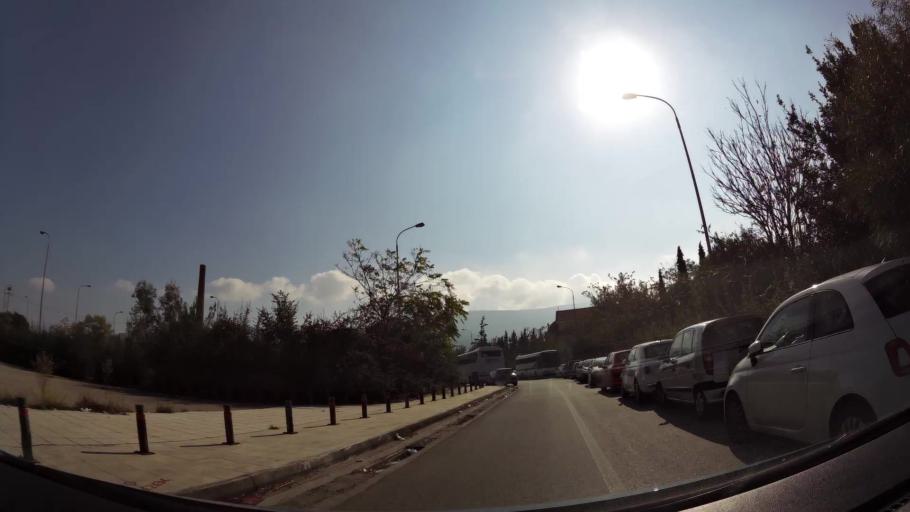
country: GR
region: Attica
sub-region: Nomarchia Athinas
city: Papagou
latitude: 37.9853
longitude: 23.7751
